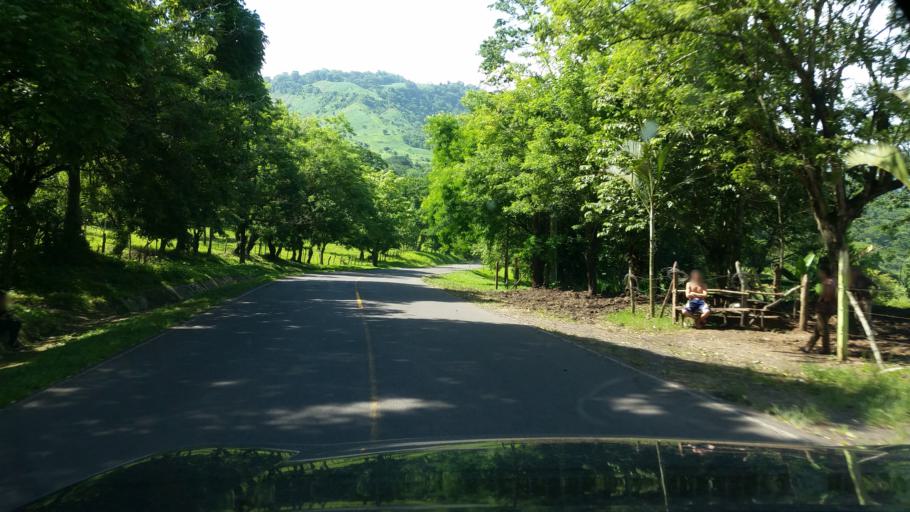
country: NI
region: Matagalpa
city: San Ramon
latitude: 13.0177
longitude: -85.7898
